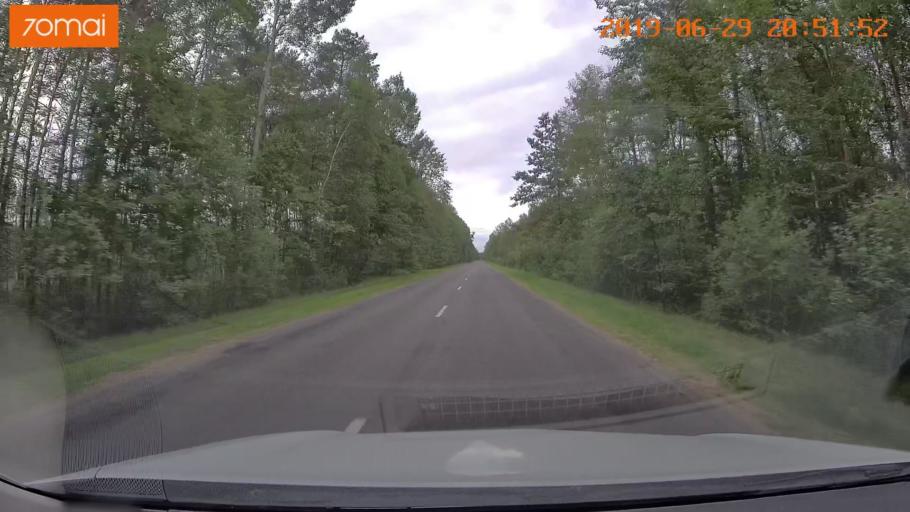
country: BY
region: Brest
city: Hantsavichy
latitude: 52.6930
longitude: 26.3553
